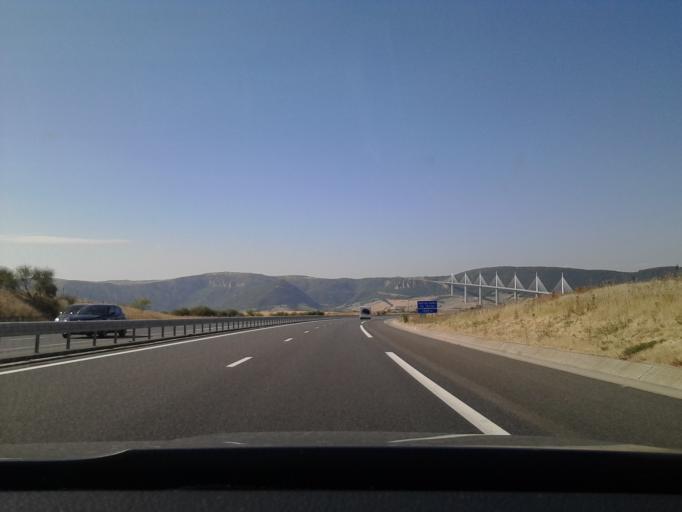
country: FR
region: Midi-Pyrenees
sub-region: Departement de l'Aveyron
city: Creissels
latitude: 44.1132
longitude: 3.0296
